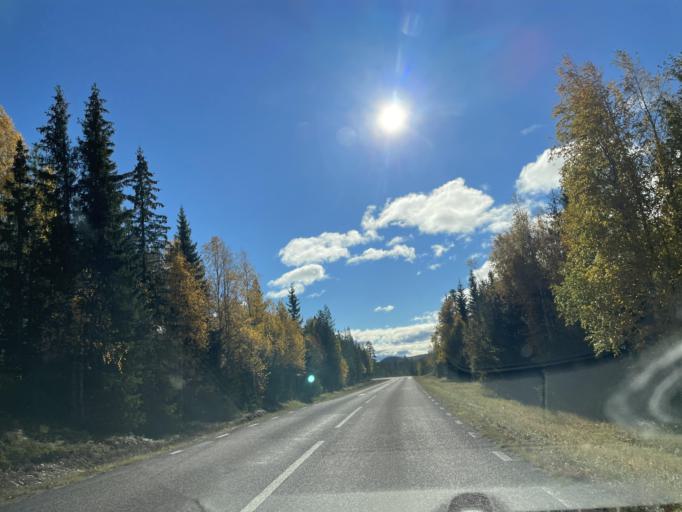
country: NO
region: Hedmark
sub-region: Trysil
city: Innbygda
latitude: 61.4491
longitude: 13.1004
